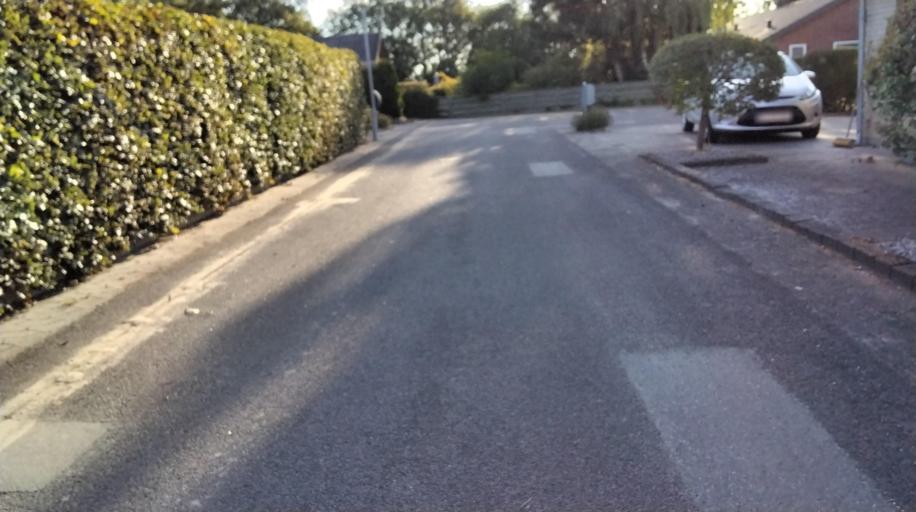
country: DK
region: Zealand
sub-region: Naestved Kommune
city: Naestved
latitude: 55.2287
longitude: 11.7365
